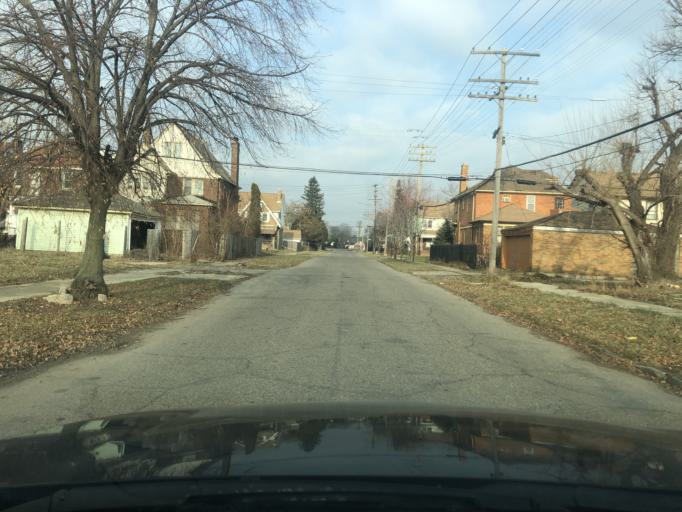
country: US
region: Michigan
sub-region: Wayne County
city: Highland Park
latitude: 42.3898
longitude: -83.1366
